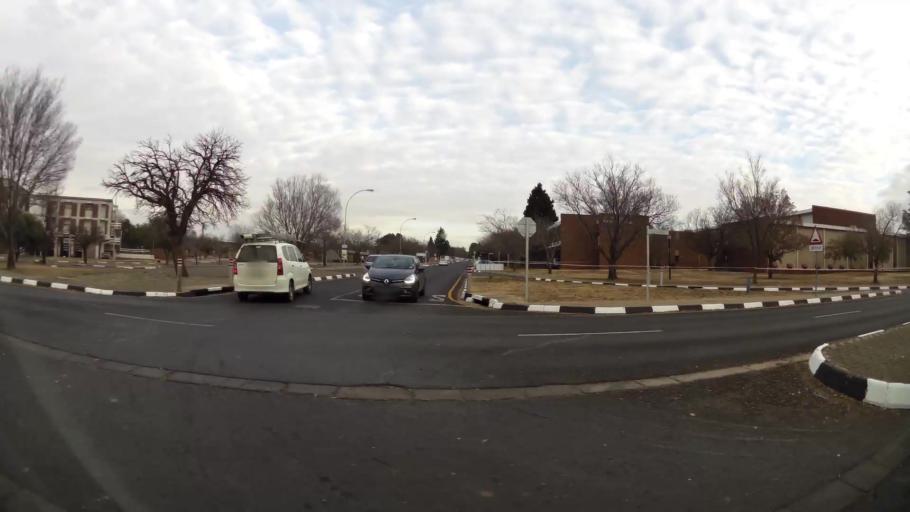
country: ZA
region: Orange Free State
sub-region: Mangaung Metropolitan Municipality
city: Bloemfontein
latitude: -29.1140
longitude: 26.1911
